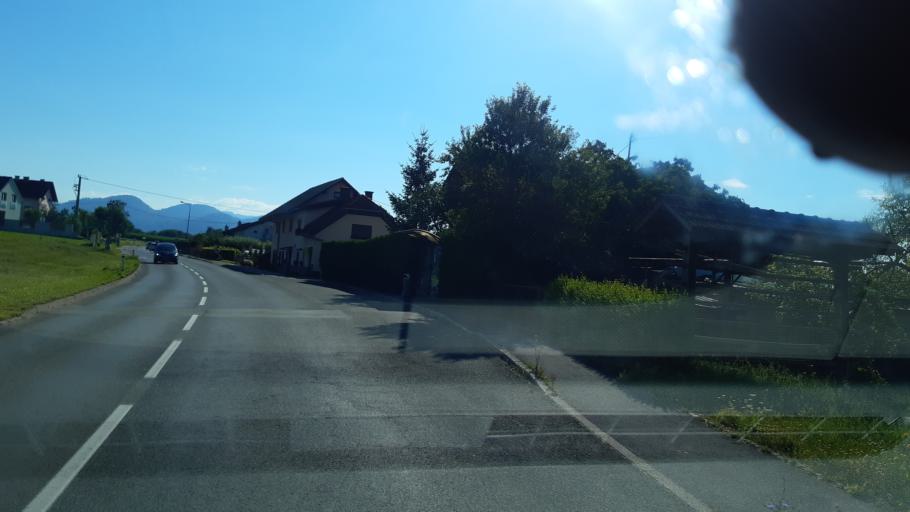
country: SI
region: Komenda
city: Moste
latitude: 46.1979
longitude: 14.5656
